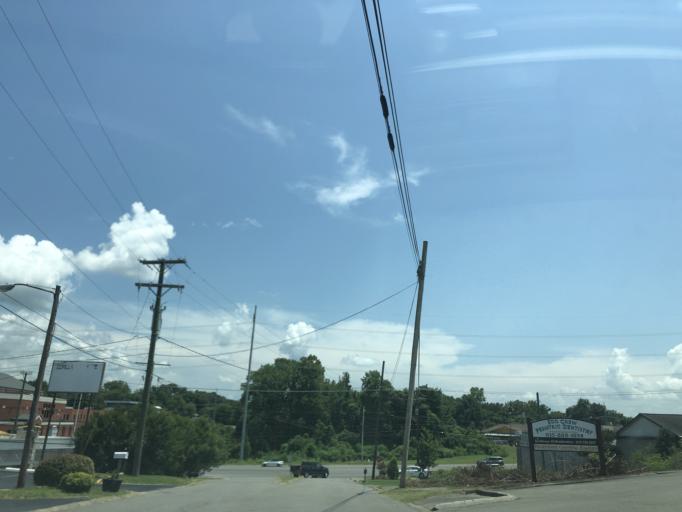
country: US
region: Tennessee
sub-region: Davidson County
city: Lakewood
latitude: 36.1924
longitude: -86.6259
